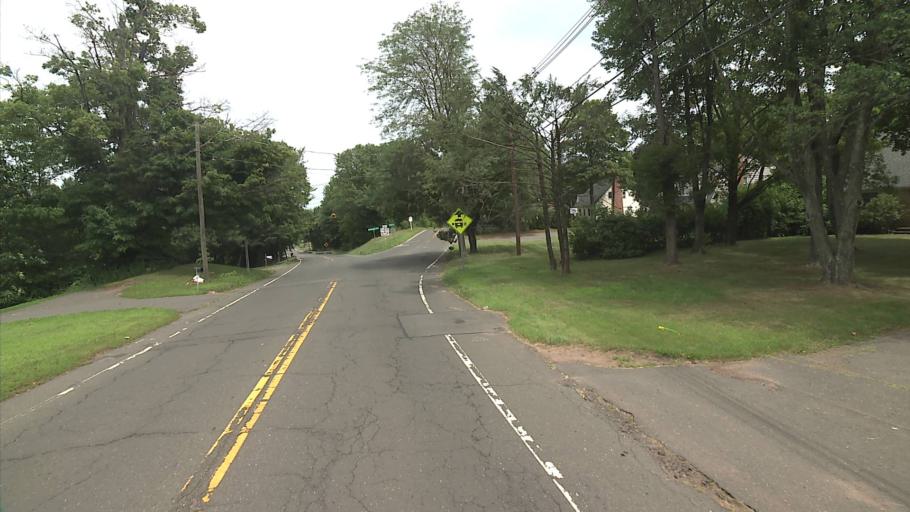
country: US
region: Connecticut
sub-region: Hartford County
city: Kensington
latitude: 41.6124
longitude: -72.7935
